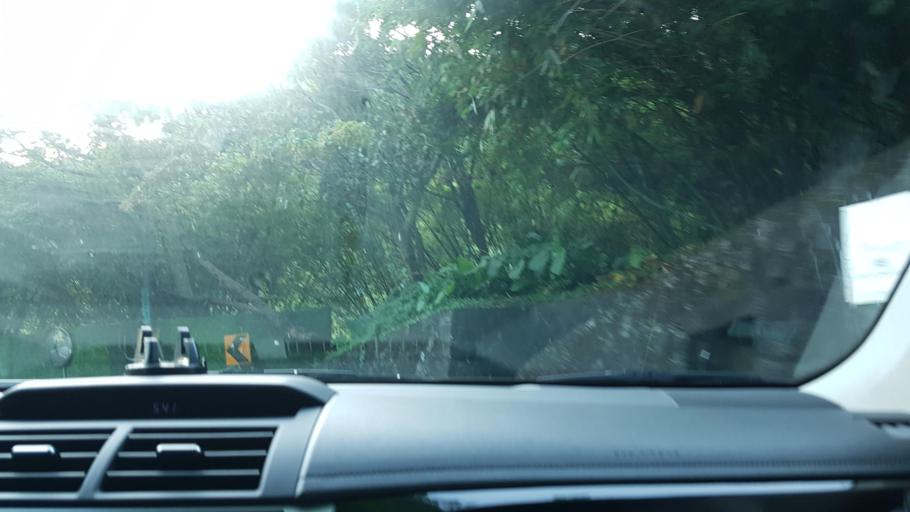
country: TW
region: Taipei
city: Taipei
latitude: 25.1149
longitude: 121.5673
